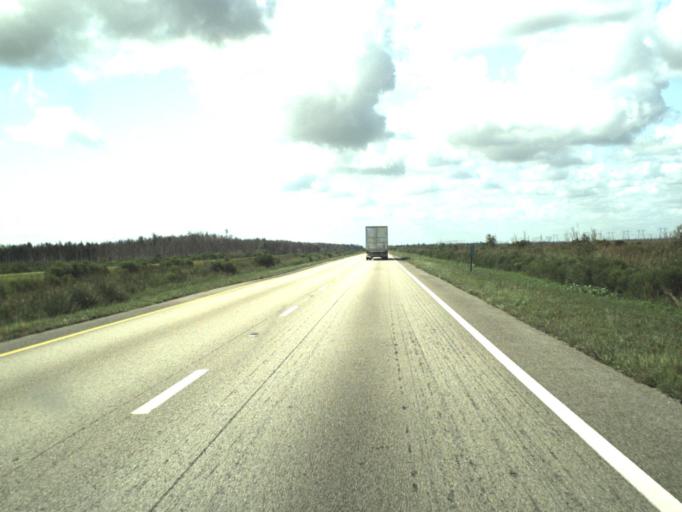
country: US
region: Florida
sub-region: Miami-Dade County
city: Palm Springs North
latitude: 25.9910
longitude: -80.4324
